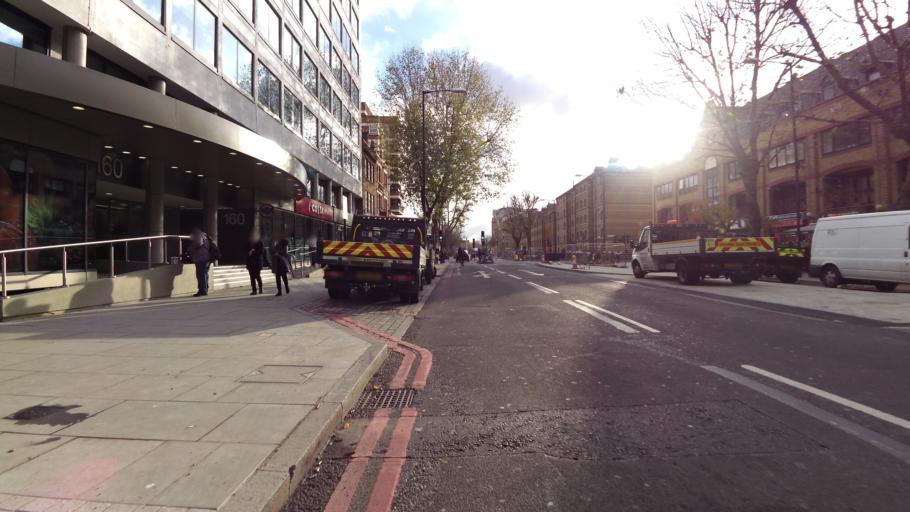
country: GB
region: England
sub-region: Greater London
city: Lambeth
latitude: 51.5015
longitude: -0.1046
